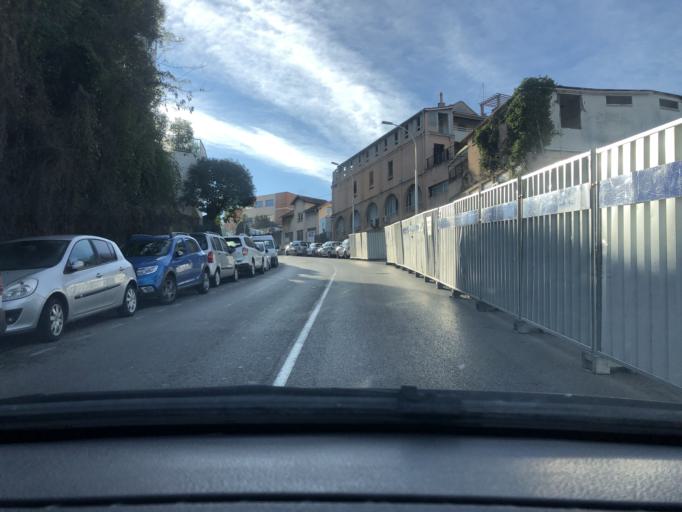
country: FR
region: Provence-Alpes-Cote d'Azur
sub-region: Departement des Alpes-Maritimes
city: Saint-Laurent-du-Var
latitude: 43.6763
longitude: 7.2083
